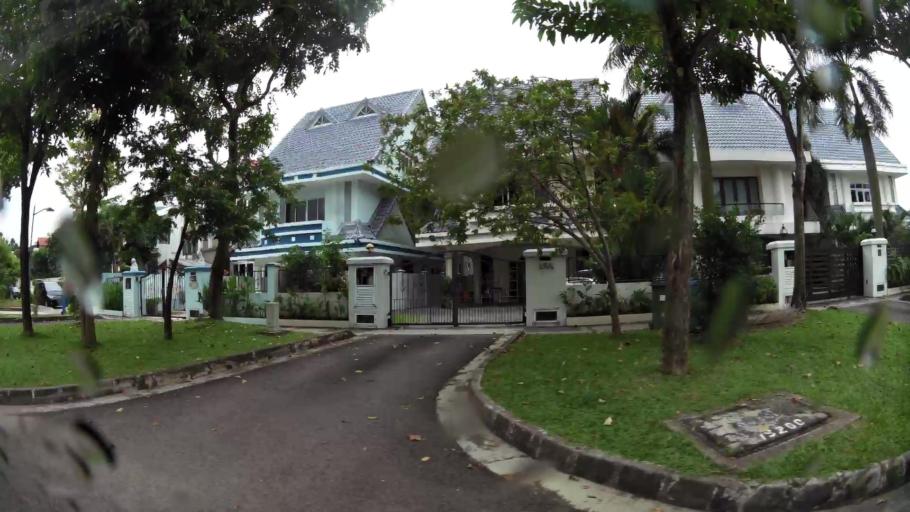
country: SG
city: Singapore
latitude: 1.3632
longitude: 103.8718
